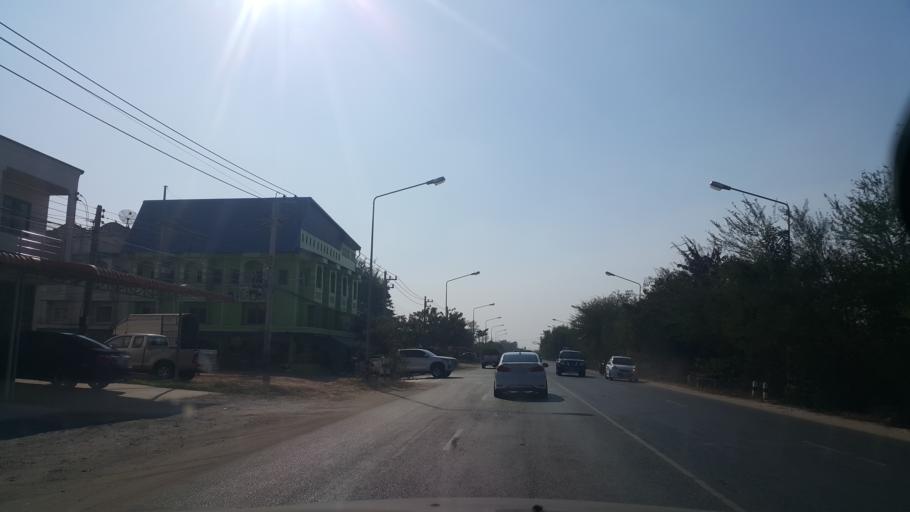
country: TH
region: Nakhon Ratchasima
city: Phimai
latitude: 15.2146
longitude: 102.4834
